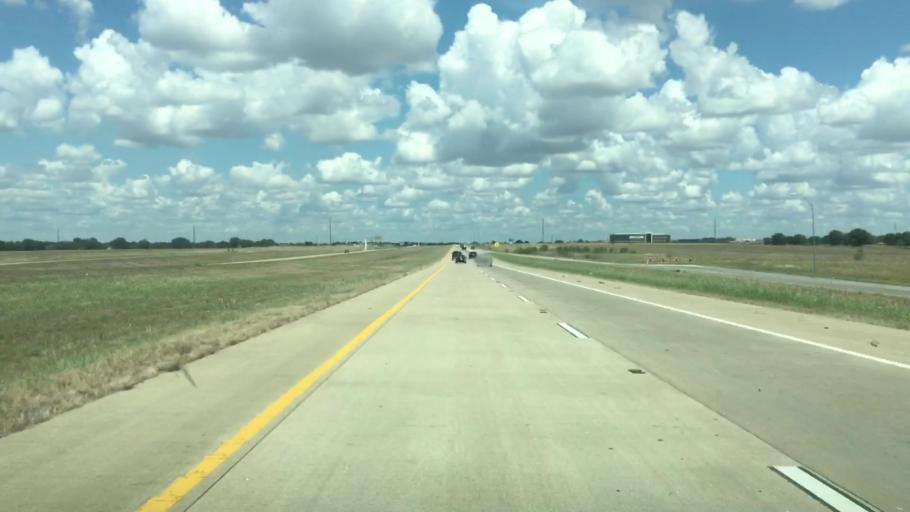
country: US
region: Texas
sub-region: Williamson County
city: Hutto
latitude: 30.5415
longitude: -97.5762
